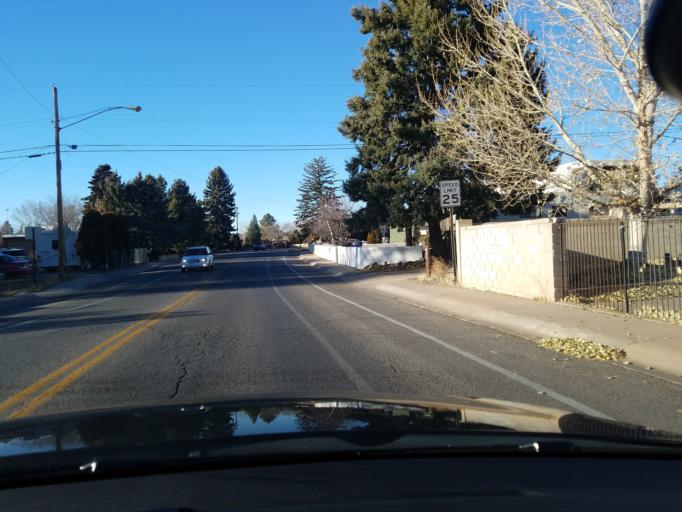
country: US
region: New Mexico
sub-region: Santa Fe County
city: Agua Fria
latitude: 35.6676
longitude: -105.9793
